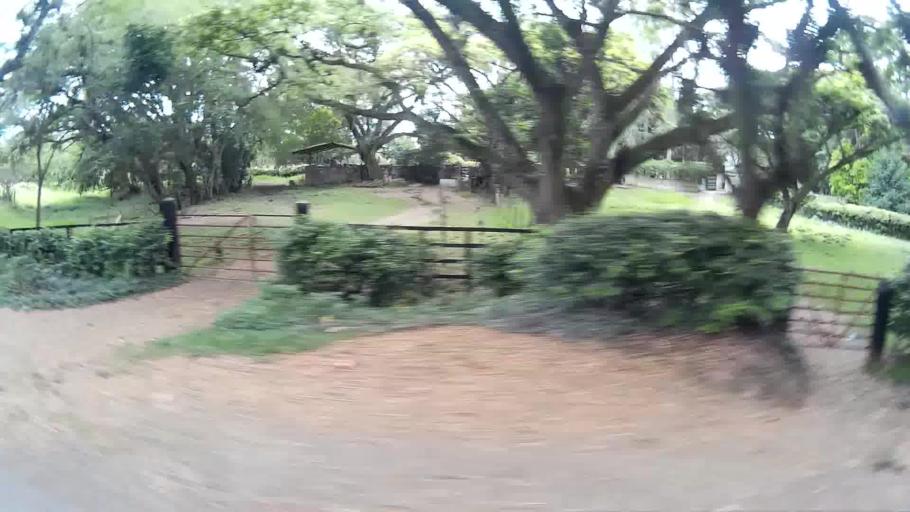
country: CO
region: Risaralda
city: La Virginia
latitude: 4.8922
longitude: -75.8775
